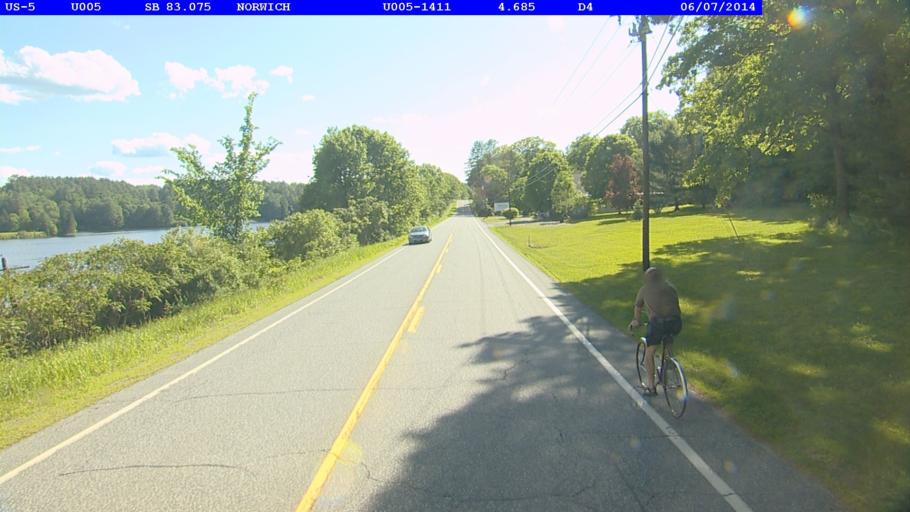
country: US
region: New Hampshire
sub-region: Grafton County
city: Hanover
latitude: 43.7378
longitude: -72.2574
